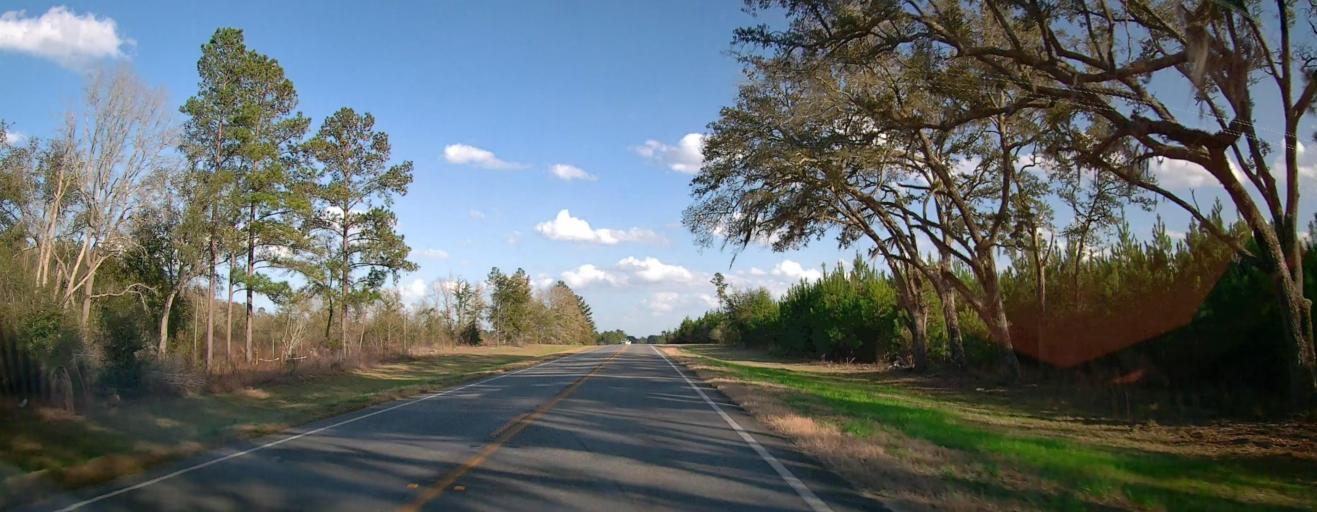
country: US
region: Georgia
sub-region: Tattnall County
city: Reidsville
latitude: 32.1238
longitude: -82.2030
